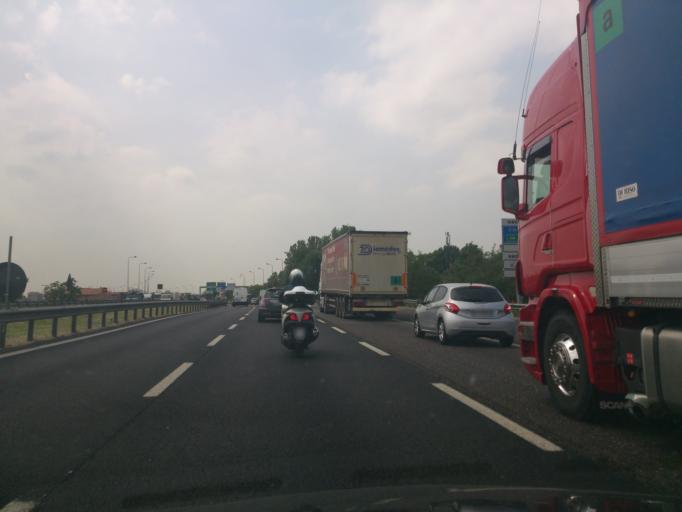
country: IT
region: Lombardy
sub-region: Citta metropolitana di Milano
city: Novegro-Tregarezzo-San Felice
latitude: 45.4941
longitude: 9.2533
